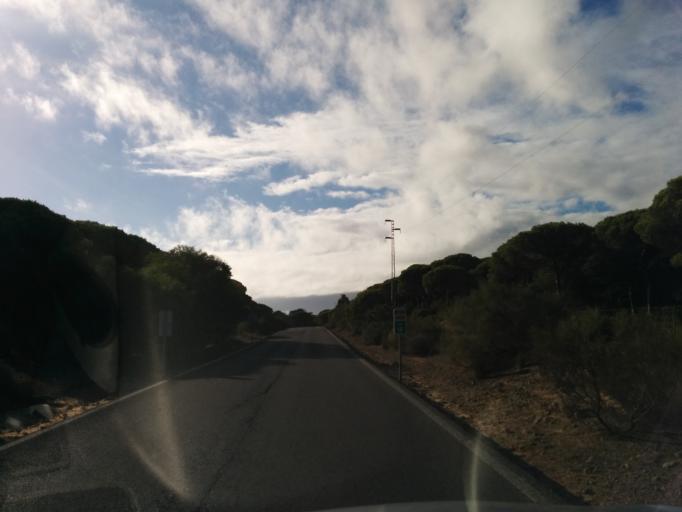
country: ES
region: Andalusia
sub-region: Provincia de Cadiz
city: Vejer de la Frontera
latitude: 36.1932
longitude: -5.9897
